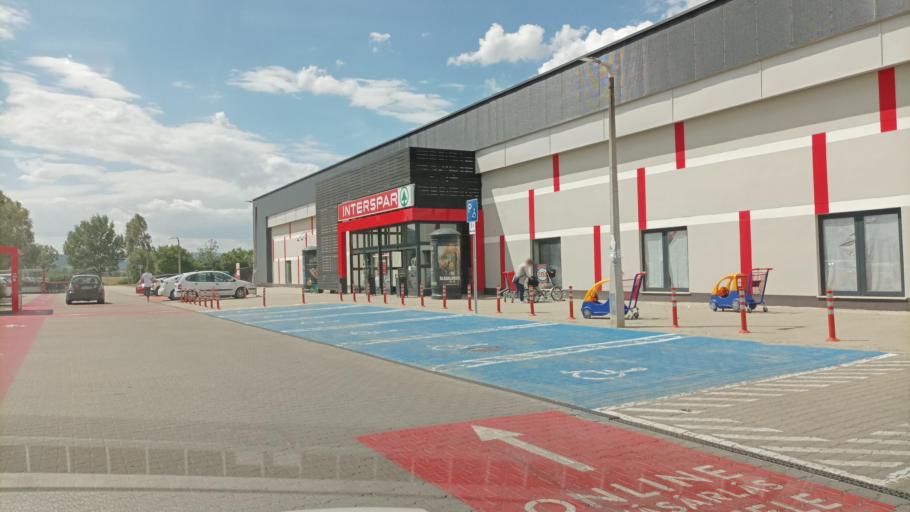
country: HU
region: Pest
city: Szentendre
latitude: 47.6461
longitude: 19.0642
